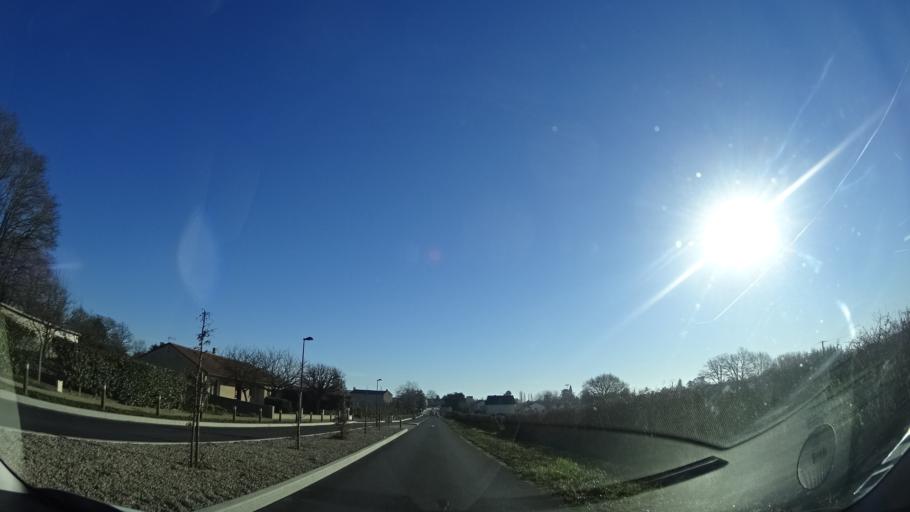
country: FR
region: Poitou-Charentes
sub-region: Departement des Deux-Sevres
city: Chiche
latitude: 46.8315
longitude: -0.3626
